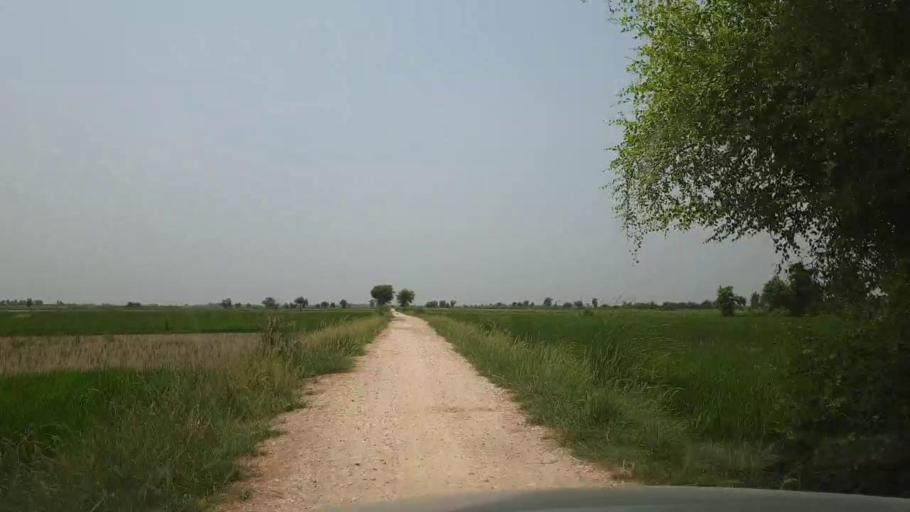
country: PK
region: Sindh
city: Garhi Yasin
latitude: 27.8667
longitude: 68.4860
